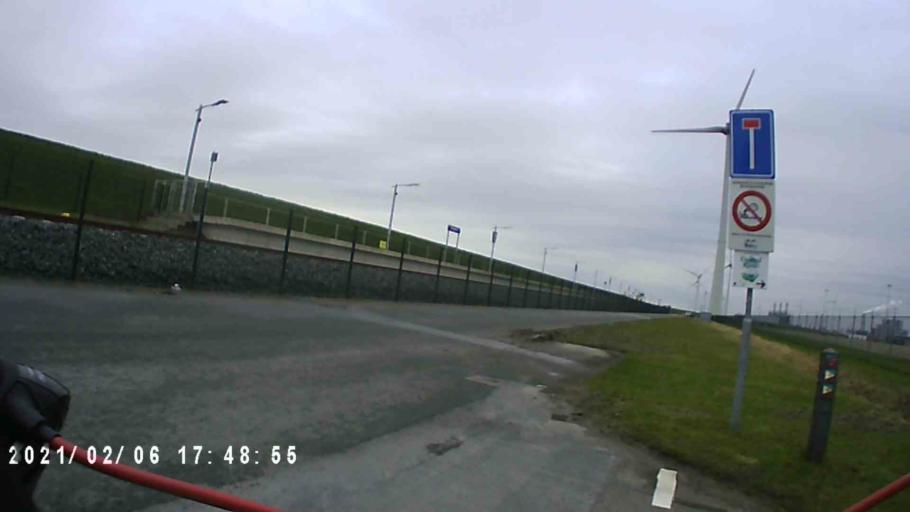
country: NL
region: Groningen
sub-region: Gemeente Appingedam
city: Appingedam
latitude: 53.4591
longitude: 6.8285
